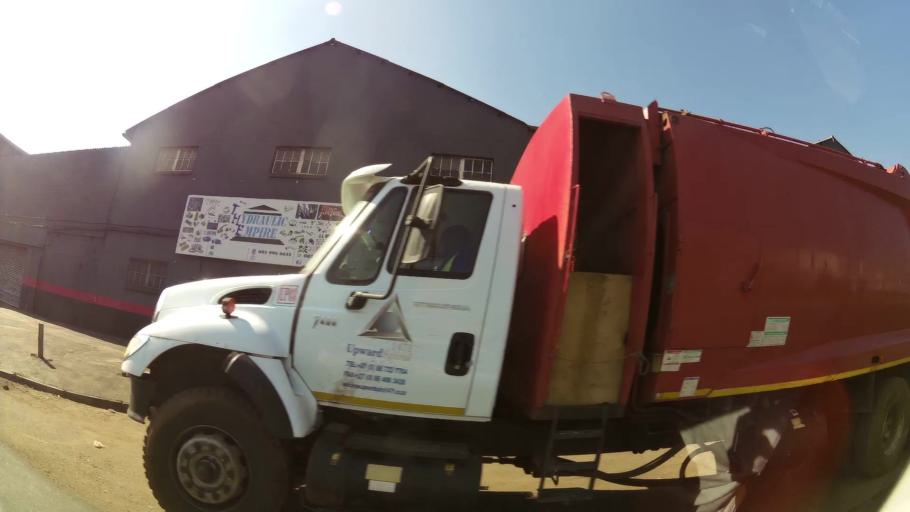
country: ZA
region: Gauteng
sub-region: Ekurhuleni Metropolitan Municipality
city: Benoni
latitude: -26.2071
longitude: 28.3062
